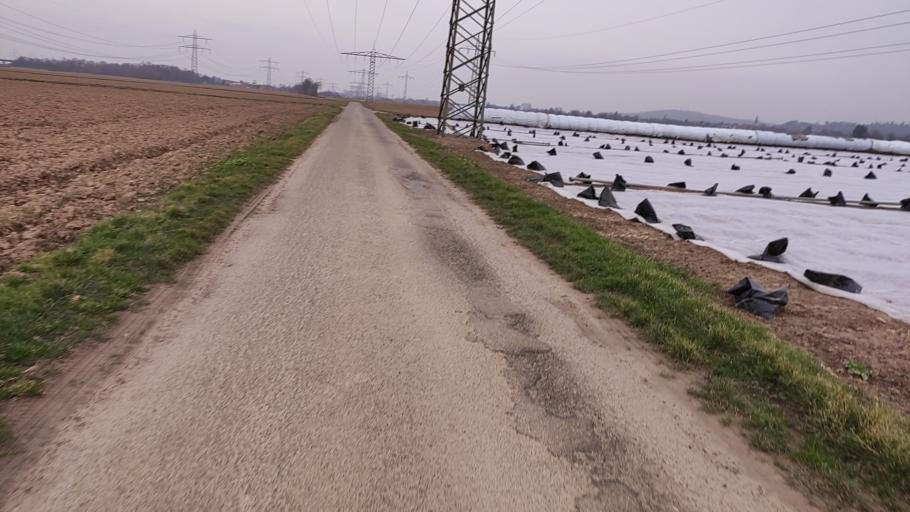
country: DE
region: Baden-Wuerttemberg
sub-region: Freiburg Region
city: Riegel
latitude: 48.1724
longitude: 7.7560
